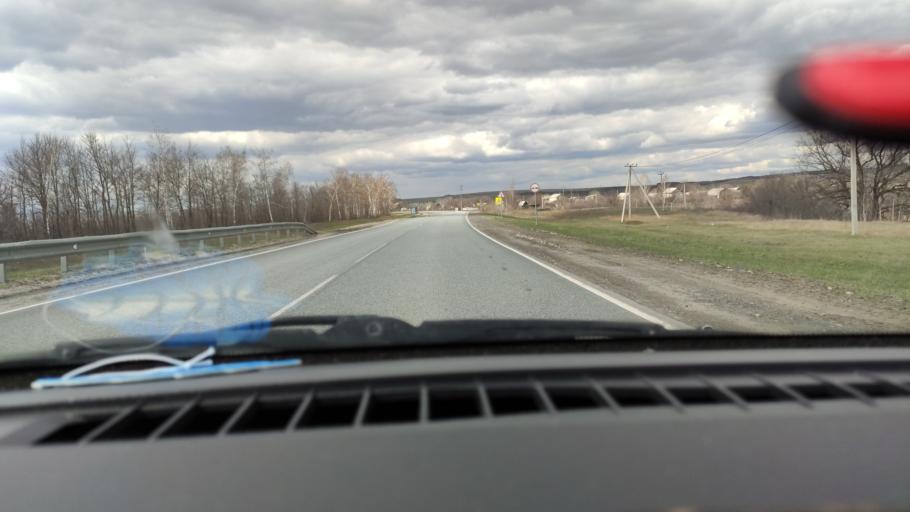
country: RU
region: Saratov
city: Tersa
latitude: 52.0867
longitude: 47.6085
